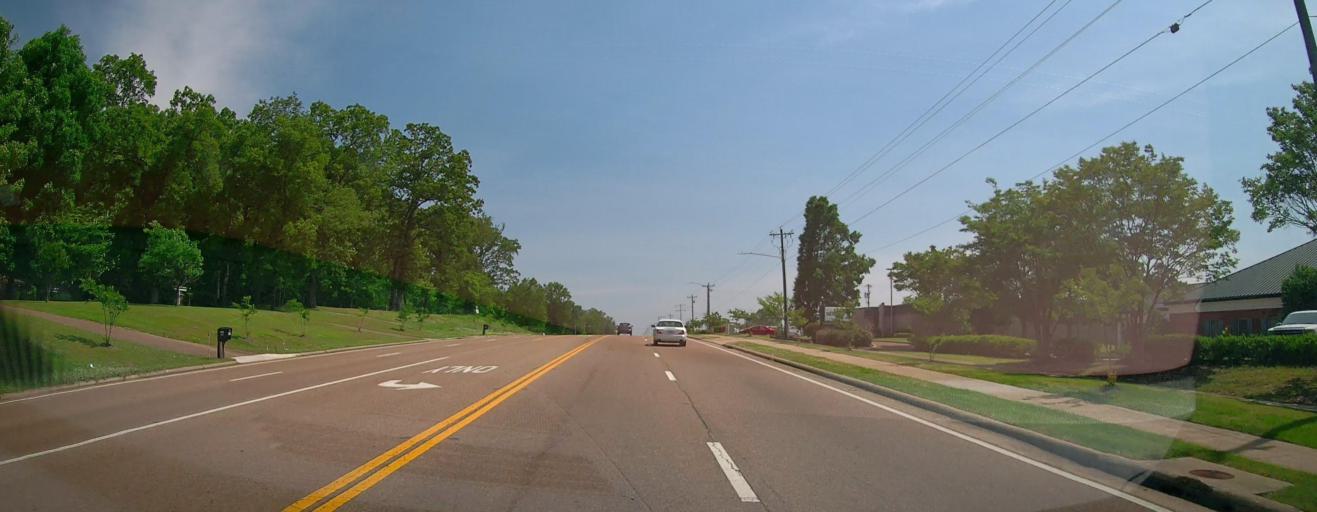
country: US
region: Mississippi
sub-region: De Soto County
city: Olive Branch
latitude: 34.9579
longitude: -89.8304
